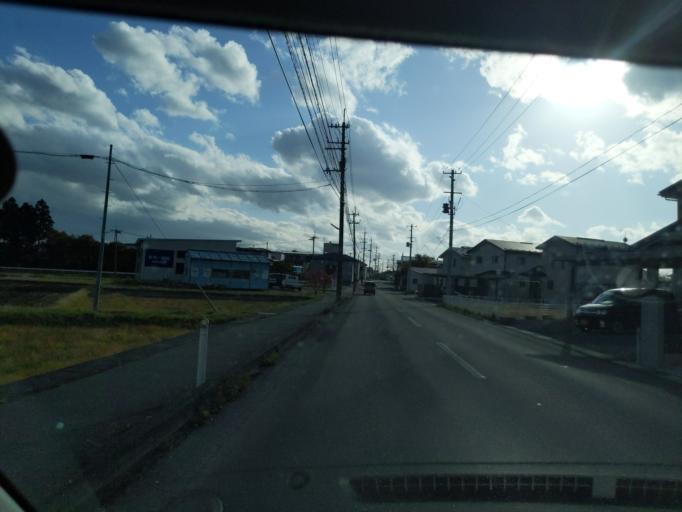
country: JP
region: Iwate
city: Mizusawa
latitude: 39.1426
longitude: 141.1585
